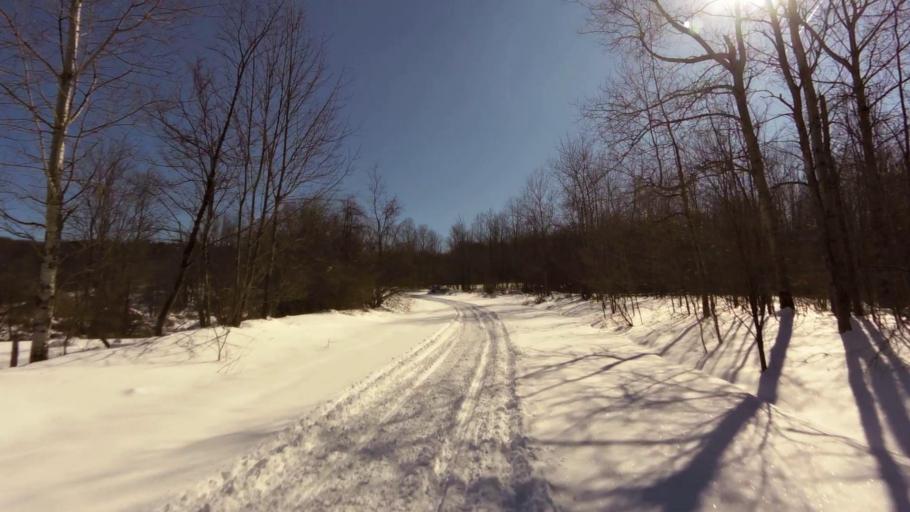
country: US
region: New York
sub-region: Allegany County
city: Cuba
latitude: 42.3307
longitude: -78.2986
